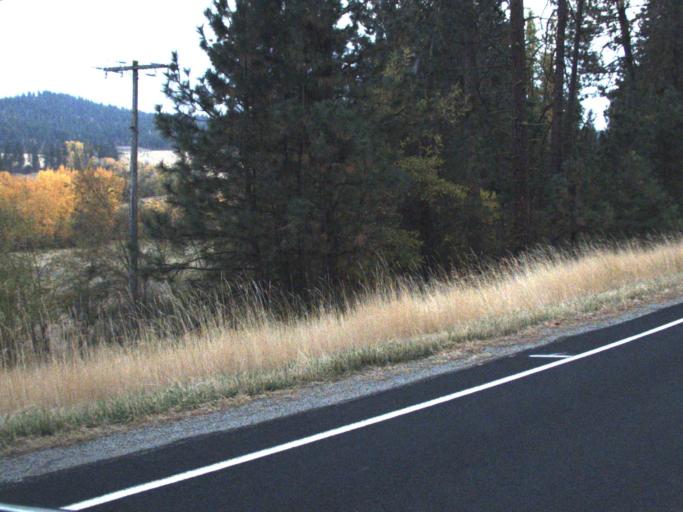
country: US
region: Washington
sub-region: Lincoln County
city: Davenport
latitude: 48.0019
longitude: -118.2756
